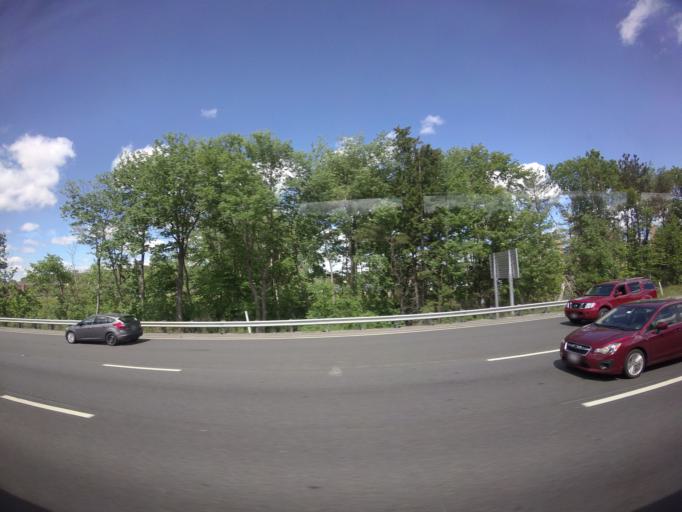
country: US
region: Massachusetts
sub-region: Middlesex County
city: Wilmington
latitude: 42.5873
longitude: -71.1604
